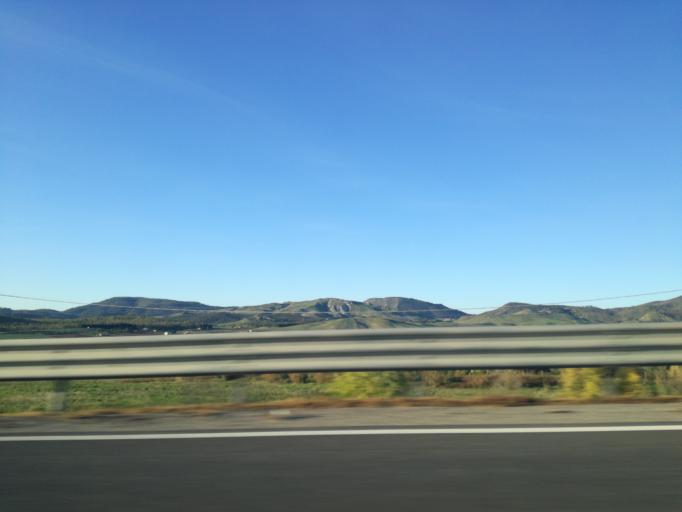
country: IT
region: Sicily
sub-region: Provincia di Caltanissetta
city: Niscemi
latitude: 37.2102
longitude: 14.3922
